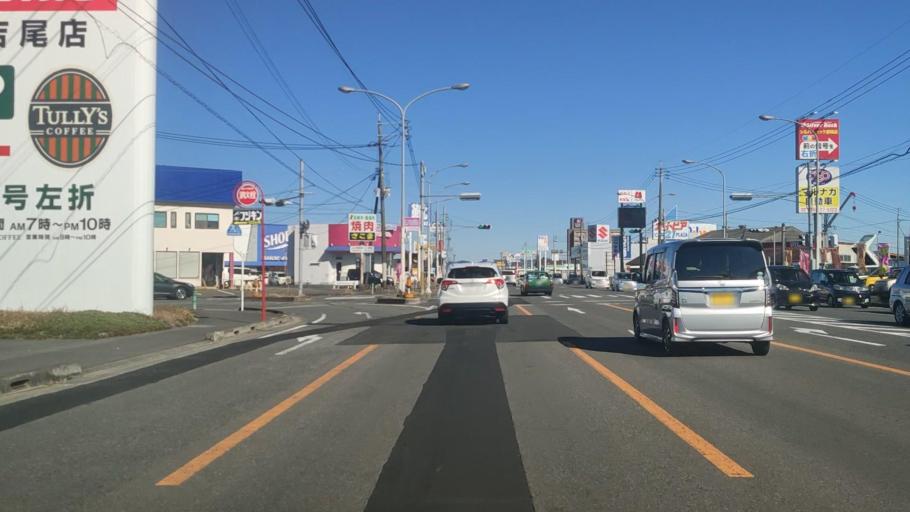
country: JP
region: Miyazaki
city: Miyakonojo
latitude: 31.7547
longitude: 131.0812
